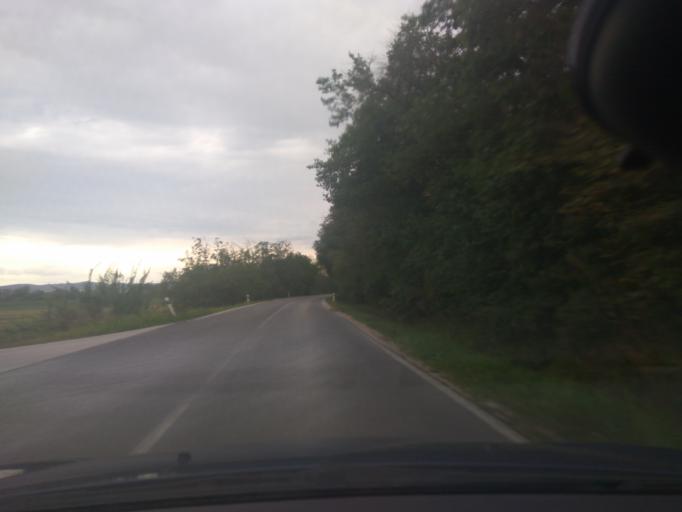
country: SK
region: Trnavsky
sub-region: Okres Trnava
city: Piestany
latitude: 48.6371
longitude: 17.8643
